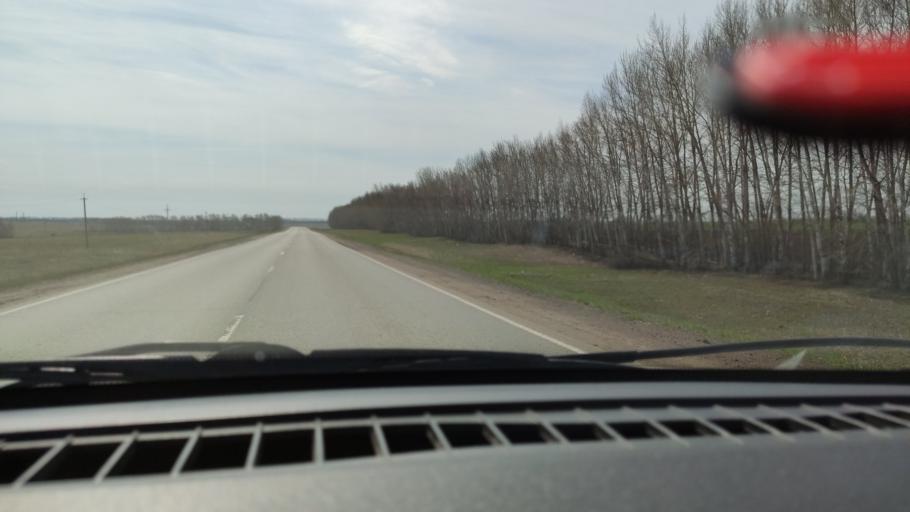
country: RU
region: Bashkortostan
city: Dyurtyuli
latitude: 55.4779
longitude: 54.7920
